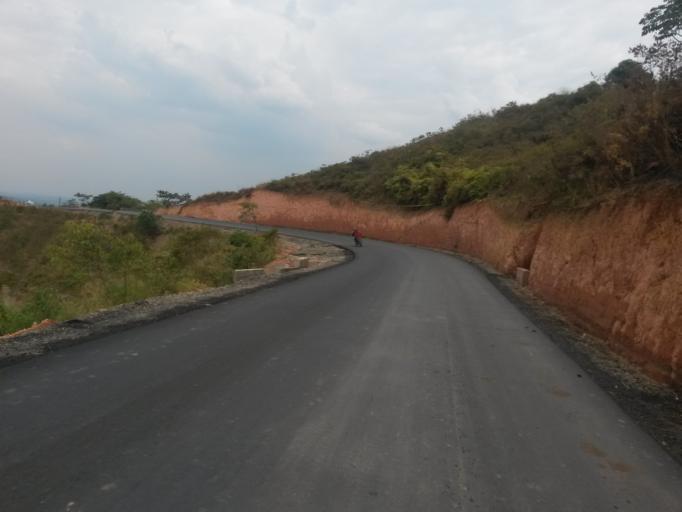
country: CO
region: Cauca
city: Buenos Aires
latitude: 3.0531
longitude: -76.6323
